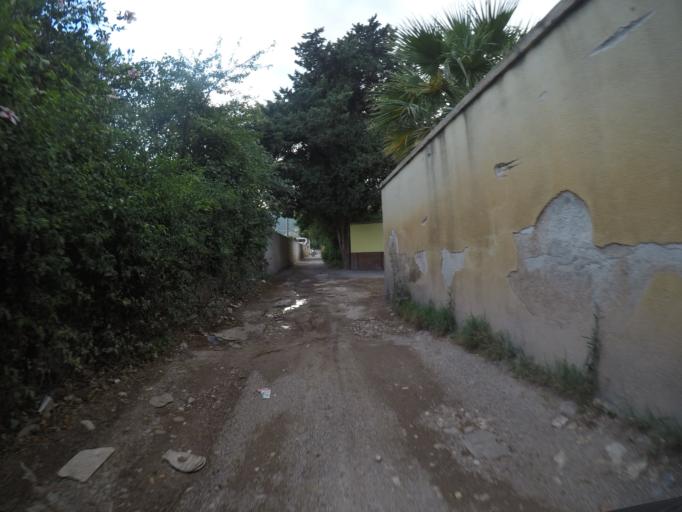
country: IT
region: Sicily
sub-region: Palermo
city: Isola delle Femmine
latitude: 38.2010
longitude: 13.3121
